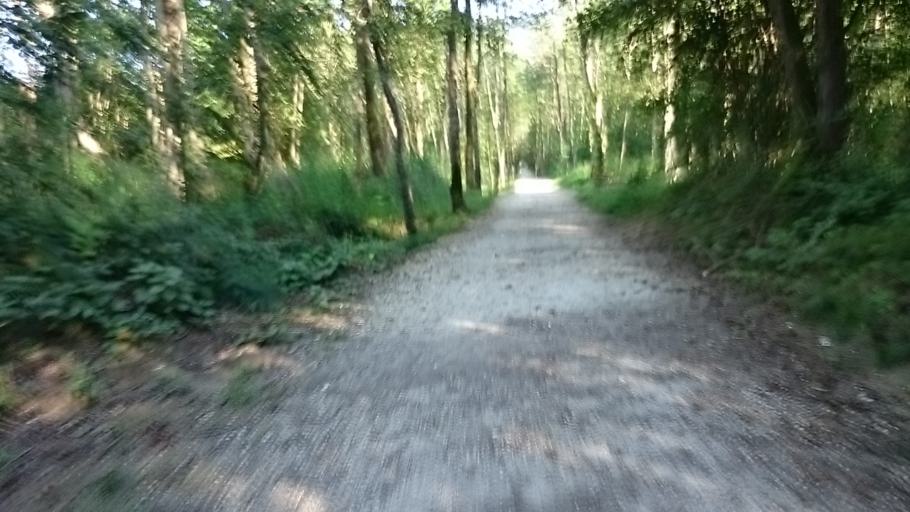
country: IT
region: Veneto
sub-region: Provincia di Belluno
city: Farra d'Alpago
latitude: 46.1236
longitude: 12.3445
